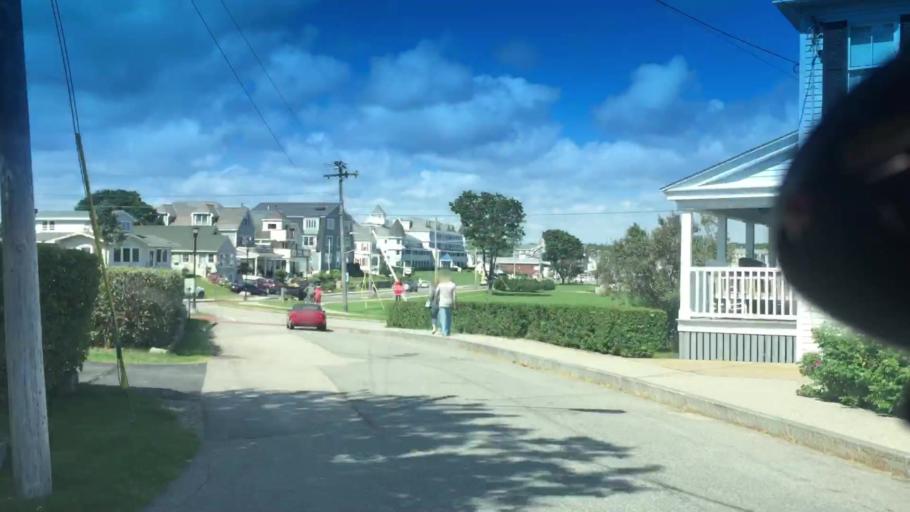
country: US
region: Maine
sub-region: York County
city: York Beach
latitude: 43.1725
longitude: -70.6061
